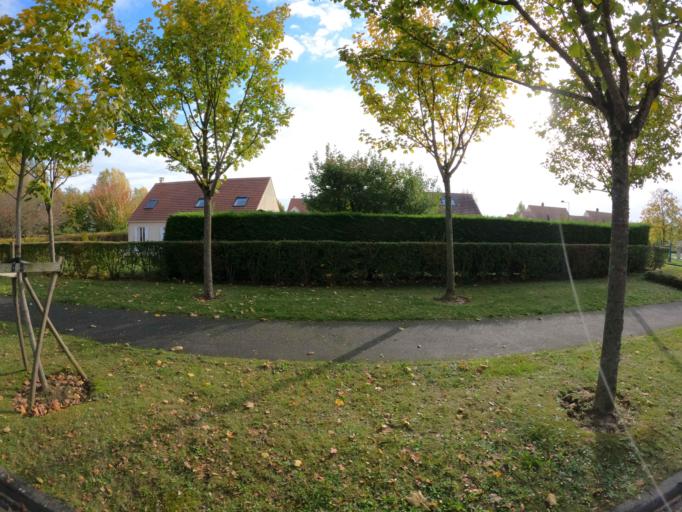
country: FR
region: Ile-de-France
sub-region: Departement de Seine-et-Marne
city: Magny-le-Hongre
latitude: 48.8620
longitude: 2.8228
